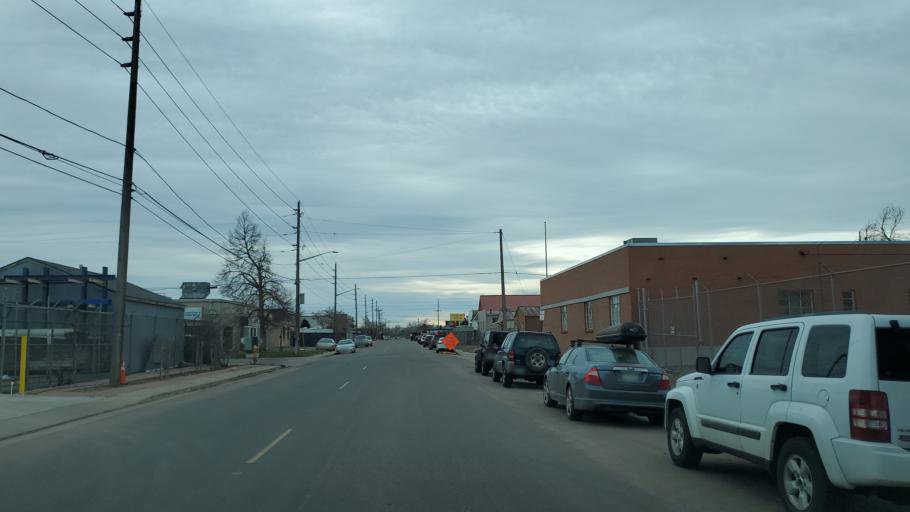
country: US
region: Colorado
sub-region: Denver County
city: Denver
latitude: 39.6954
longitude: -104.9992
